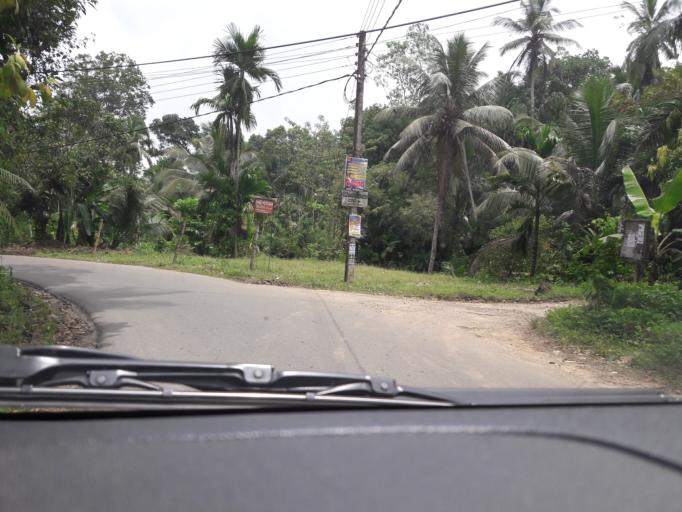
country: LK
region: Southern
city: Galle
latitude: 6.1756
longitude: 80.2882
